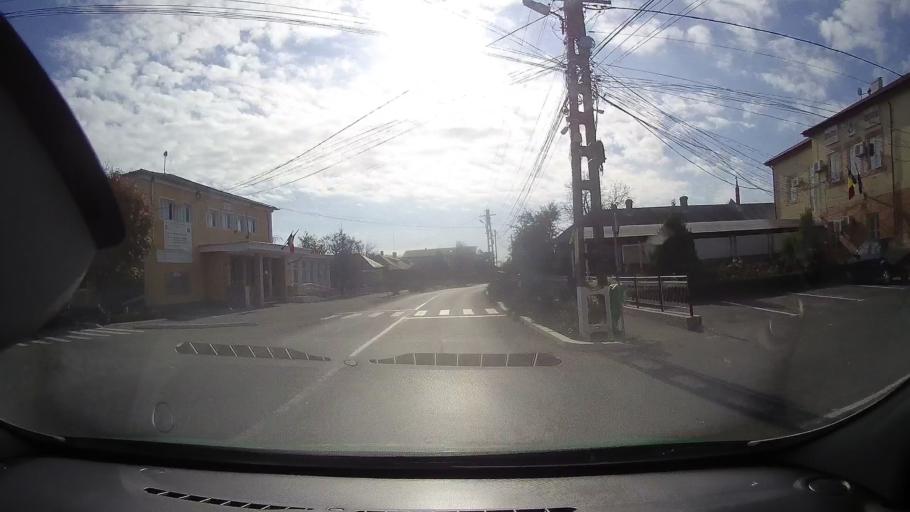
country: RO
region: Tulcea
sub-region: Comuna Sarichioi
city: Sarichioi
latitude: 44.9447
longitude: 28.8535
